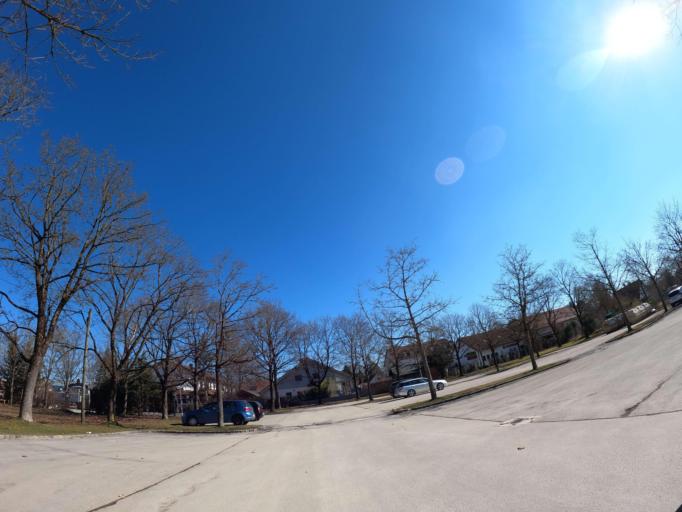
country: DE
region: Bavaria
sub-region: Upper Bavaria
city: Unterhaching
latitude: 48.1005
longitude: 11.6245
